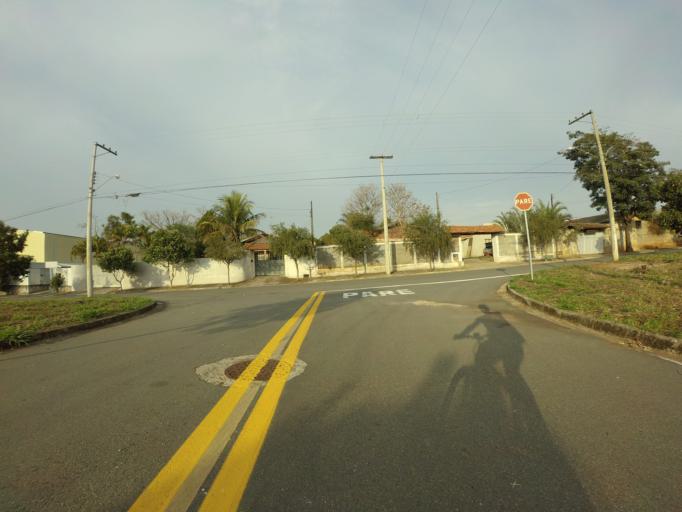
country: BR
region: Sao Paulo
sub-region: Piracicaba
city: Piracicaba
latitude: -22.7450
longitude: -47.5921
